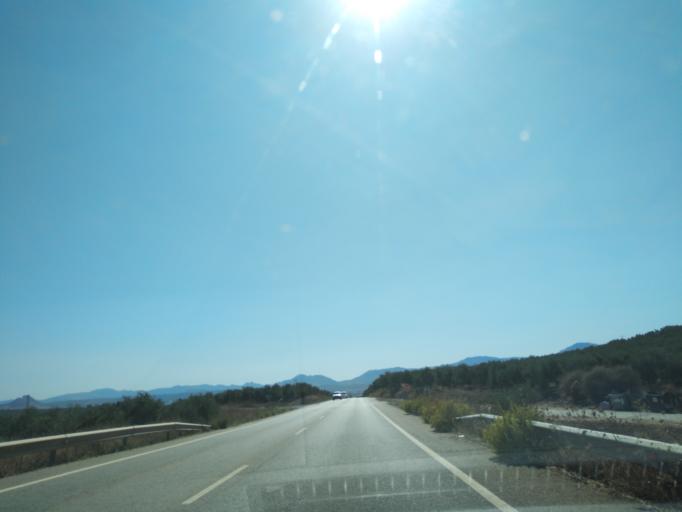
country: ES
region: Andalusia
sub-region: Provincia de Malaga
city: Mollina
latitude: 37.1083
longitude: -4.6407
